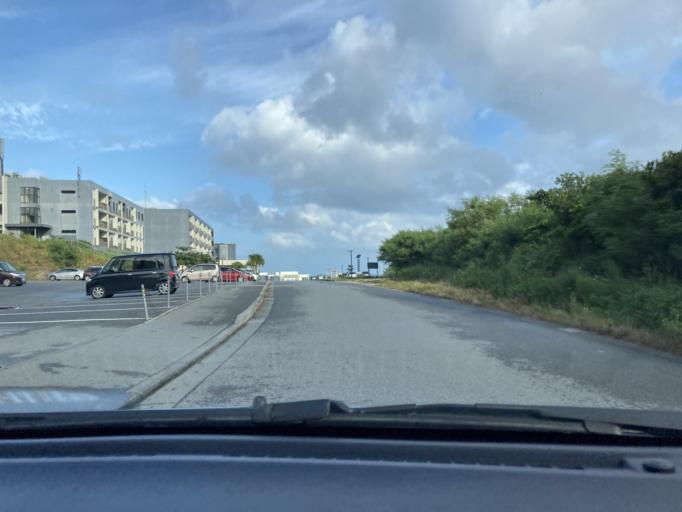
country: JP
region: Okinawa
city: Tomigusuku
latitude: 26.1755
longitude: 127.6427
